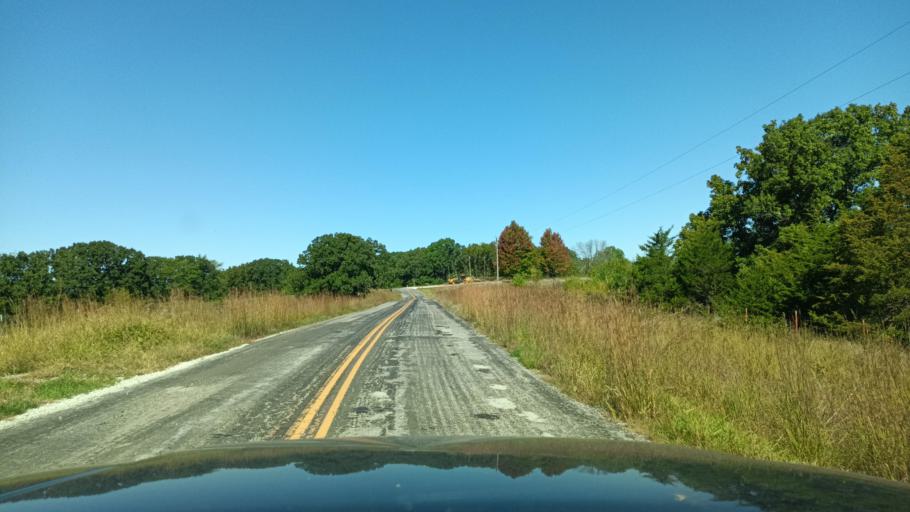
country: US
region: Missouri
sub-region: Scotland County
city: Memphis
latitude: 40.3576
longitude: -92.3589
